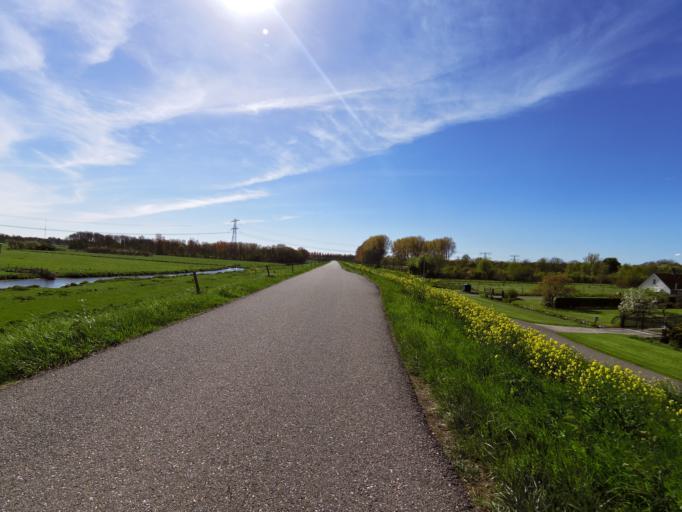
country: NL
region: South Holland
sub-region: Gemeente Brielle
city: Brielle
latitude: 51.9199
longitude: 4.1218
